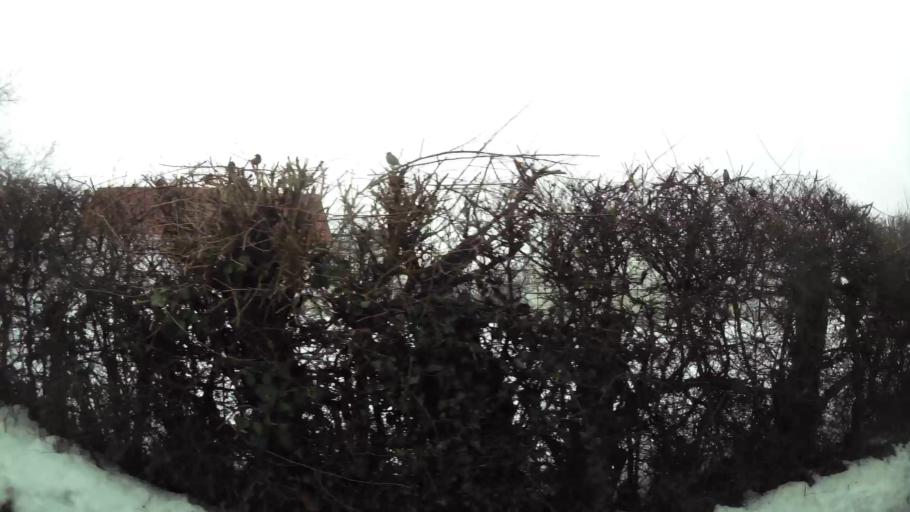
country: RS
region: Central Serbia
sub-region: Belgrade
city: Zvezdara
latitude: 44.7454
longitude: 20.5115
